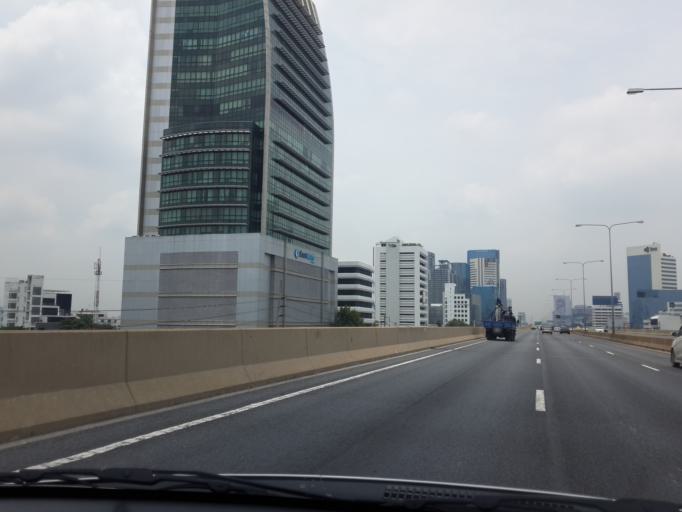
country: TH
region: Bangkok
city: Phaya Thai
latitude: 13.7983
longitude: 100.5608
